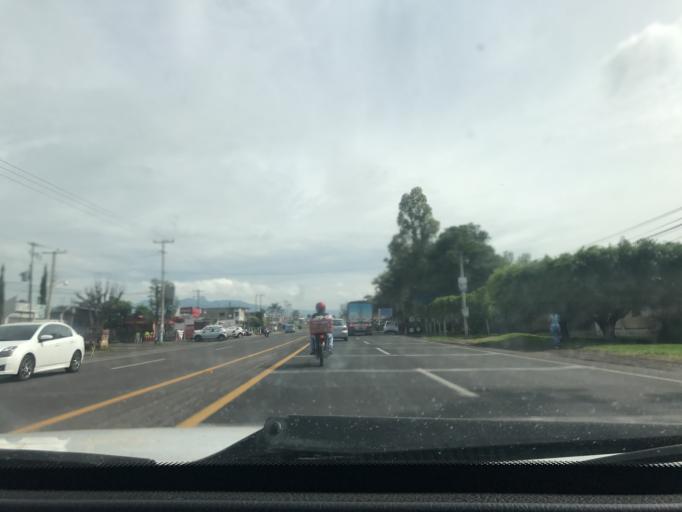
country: MX
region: Morelos
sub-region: Atlatlahucan
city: Colonia San Francisco
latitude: 18.8834
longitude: -98.9180
